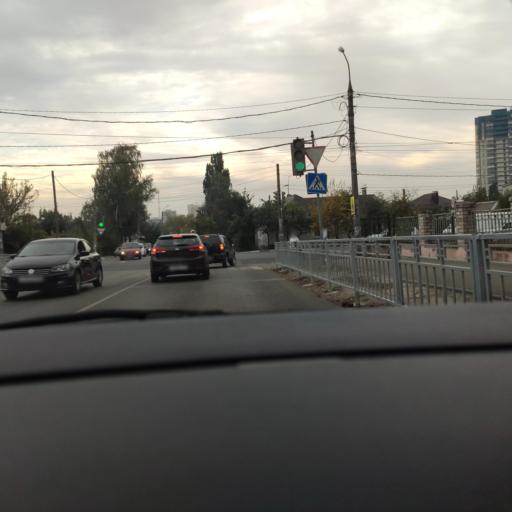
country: RU
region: Voronezj
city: Voronezh
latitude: 51.6959
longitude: 39.1898
